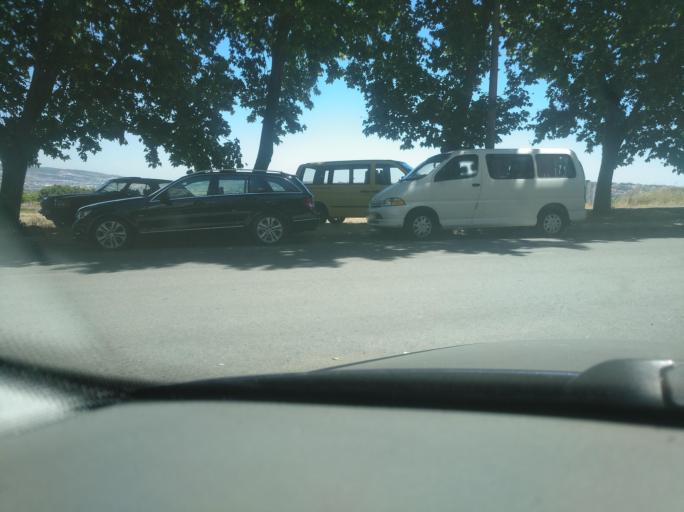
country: PT
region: Lisbon
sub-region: Odivelas
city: Povoa de Santo Adriao
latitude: 38.8119
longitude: -9.1782
